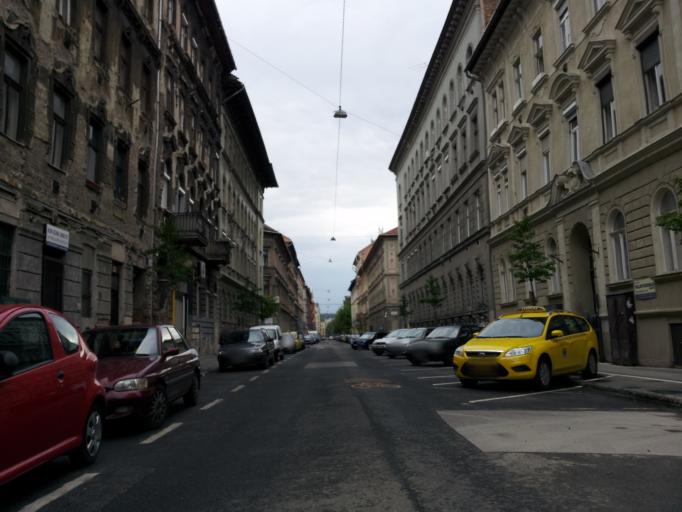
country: HU
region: Budapest
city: Budapest VII. keruelet
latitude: 47.5033
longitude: 19.0826
